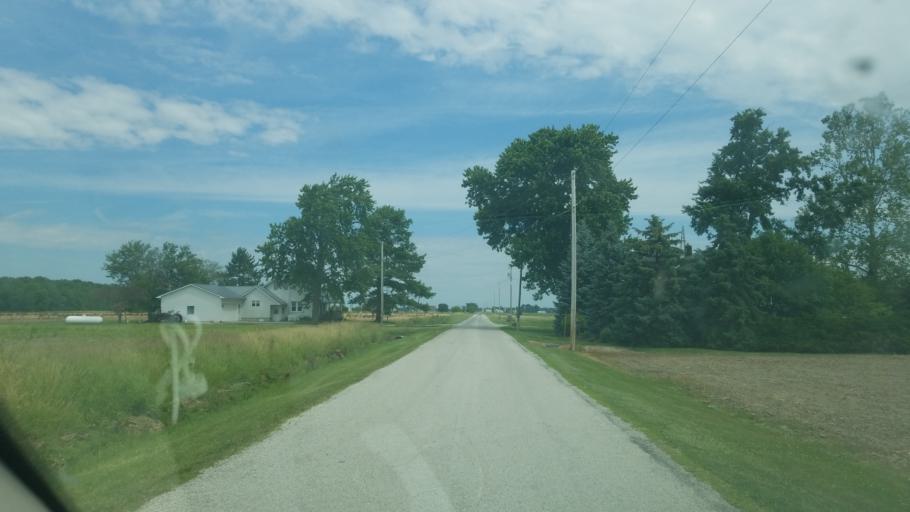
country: US
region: Ohio
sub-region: Wood County
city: North Baltimore
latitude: 41.2205
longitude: -83.5732
